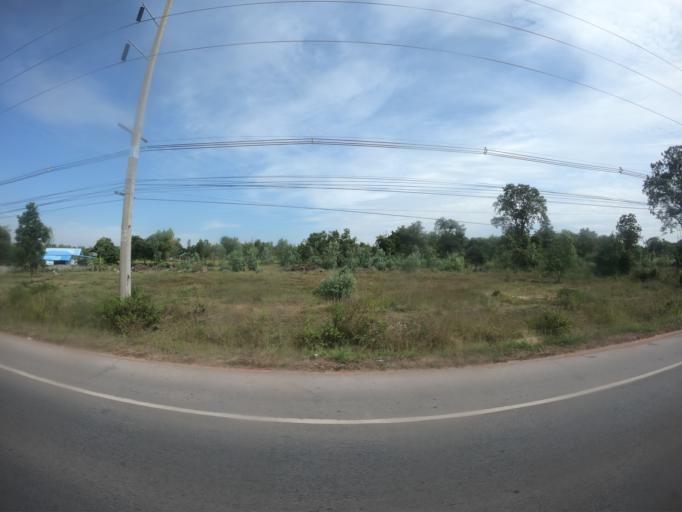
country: TH
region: Maha Sarakham
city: Chiang Yuen
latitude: 16.4434
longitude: 103.0409
